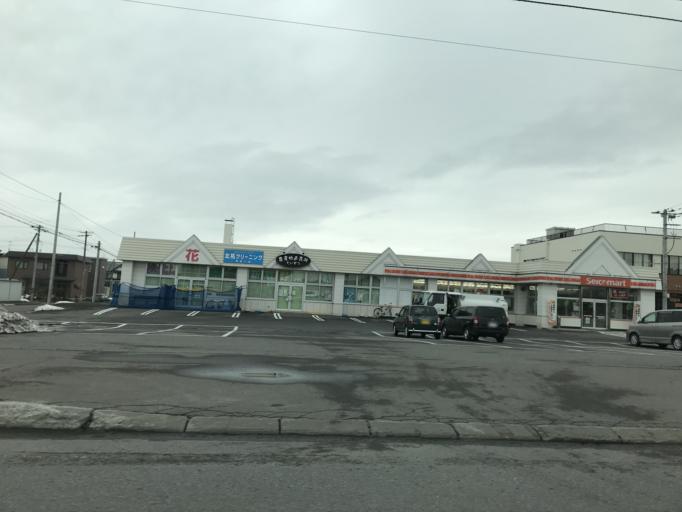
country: JP
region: Hokkaido
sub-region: Asahikawa-shi
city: Asahikawa
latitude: 43.8245
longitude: 142.4155
